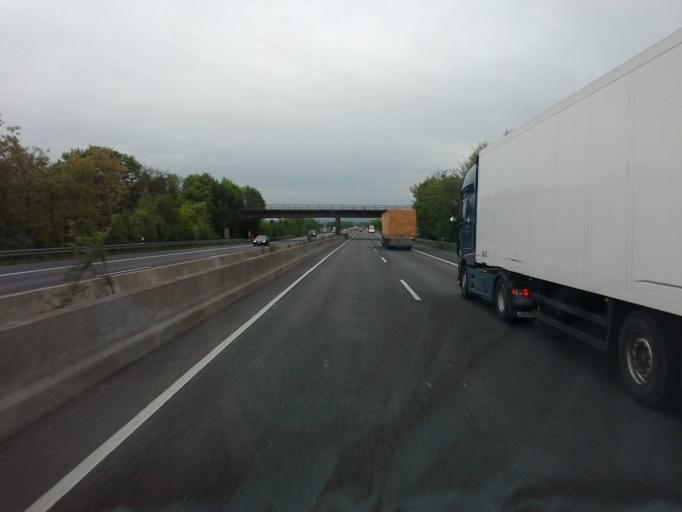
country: DE
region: North Rhine-Westphalia
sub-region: Regierungsbezirk Koln
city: Weilerswist
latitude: 50.7107
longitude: 6.9005
